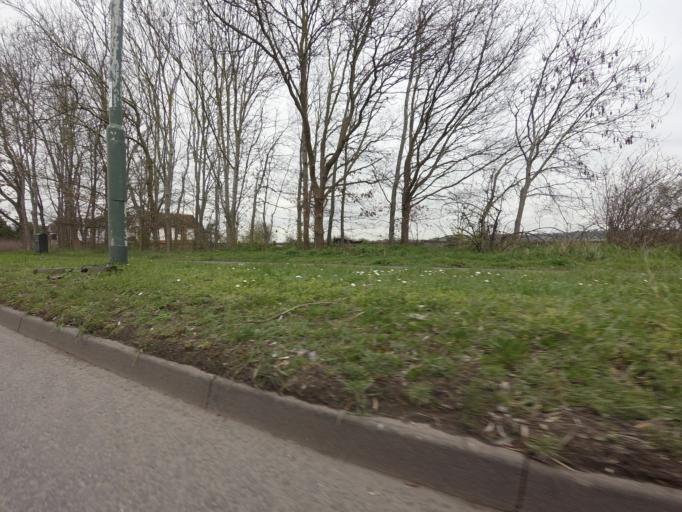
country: GB
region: England
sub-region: Greater London
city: Bexley
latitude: 51.4143
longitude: 0.1332
